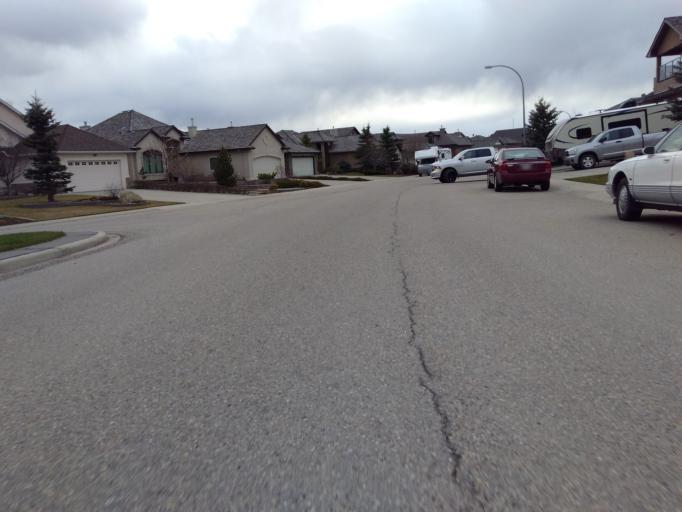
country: CA
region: Alberta
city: Cochrane
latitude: 51.1821
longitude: -114.4274
